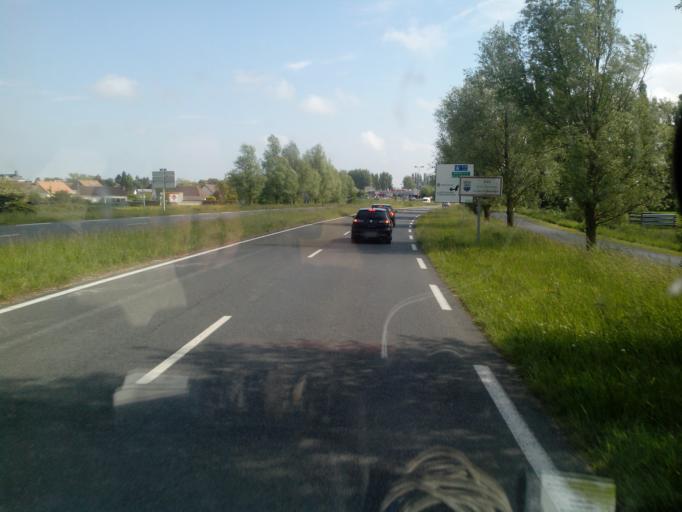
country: FR
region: Picardie
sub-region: Departement de la Somme
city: Rue
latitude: 50.2789
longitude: 1.6594
